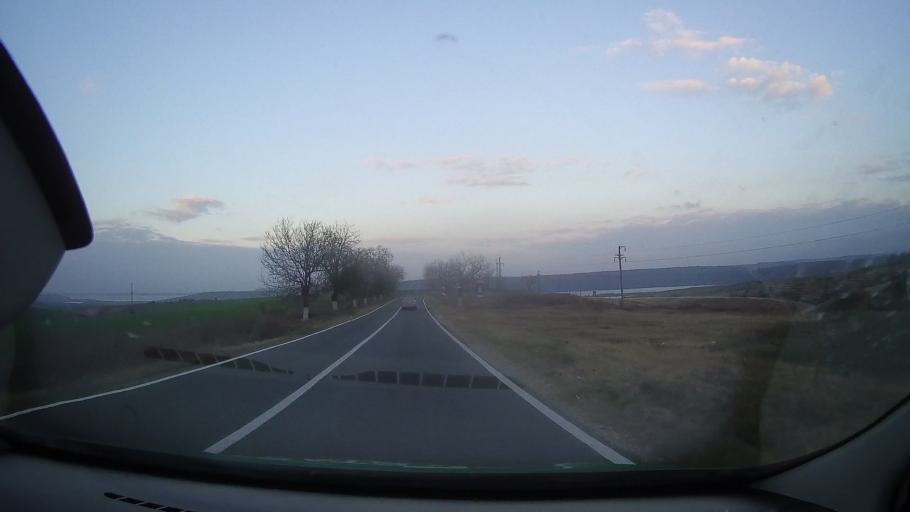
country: RO
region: Constanta
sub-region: Comuna Lipnita
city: Lipnita
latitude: 44.0955
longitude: 27.6129
